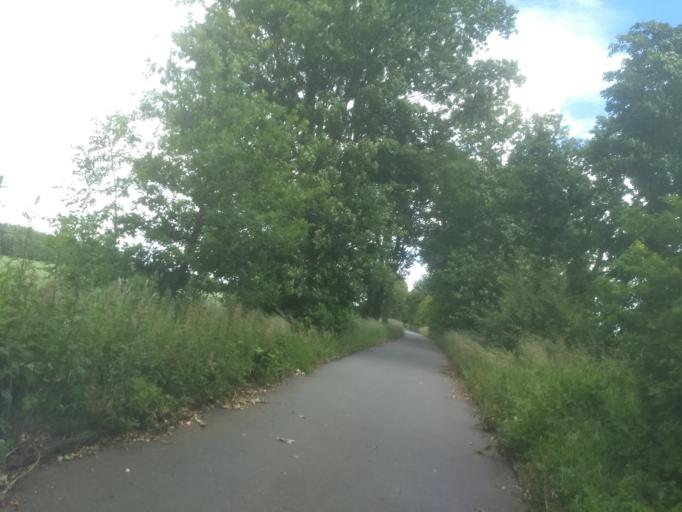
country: FR
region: Nord-Pas-de-Calais
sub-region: Departement du Pas-de-Calais
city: Beaumetz-les-Loges
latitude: 50.2344
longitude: 2.6487
